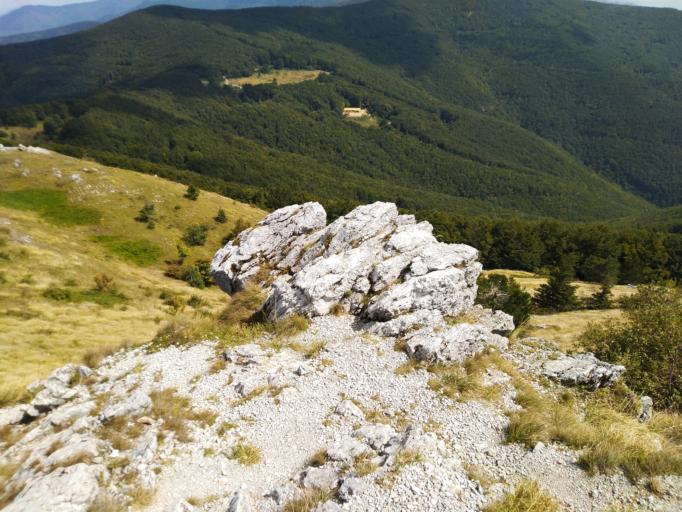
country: BG
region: Stara Zagora
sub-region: Obshtina Kazanluk
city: Shipka
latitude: 42.7474
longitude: 25.3227
